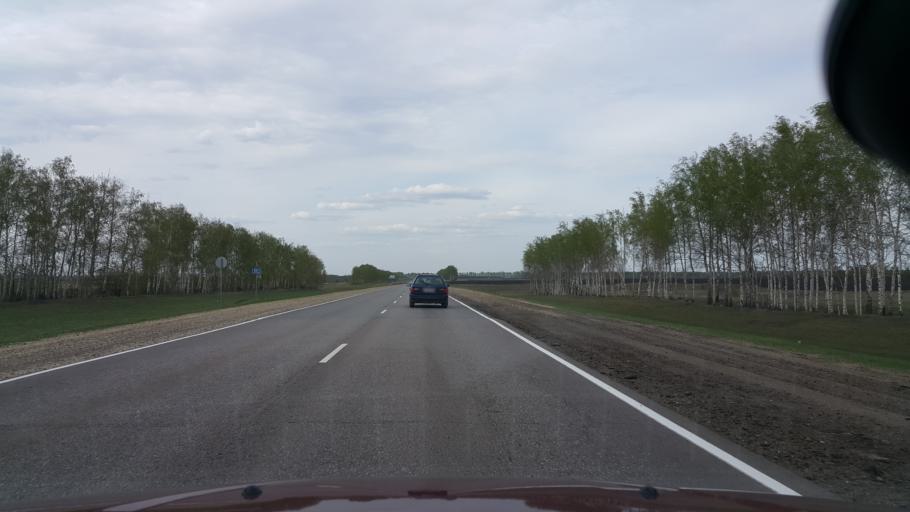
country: RU
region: Tambov
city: Pokrovo-Prigorodnoye
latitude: 52.6429
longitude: 41.3413
